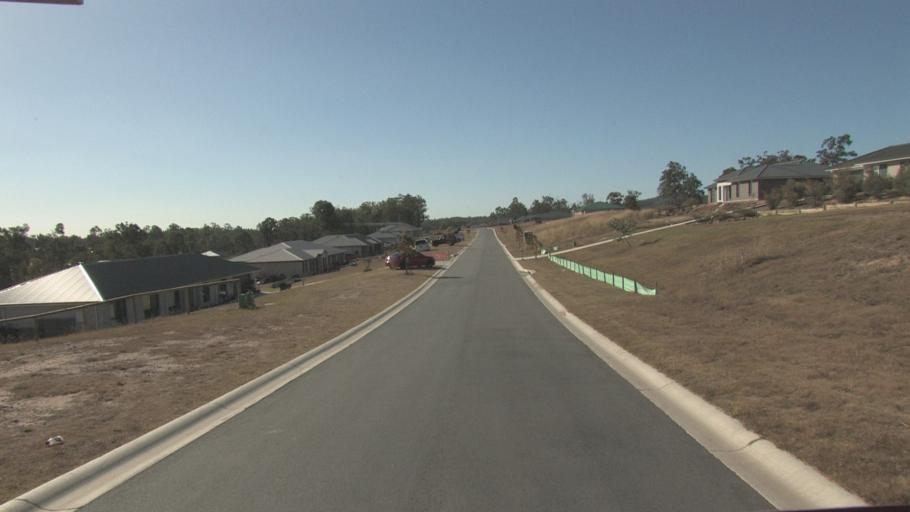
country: AU
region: Queensland
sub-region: Logan
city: Cedar Vale
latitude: -27.8703
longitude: 153.0523
